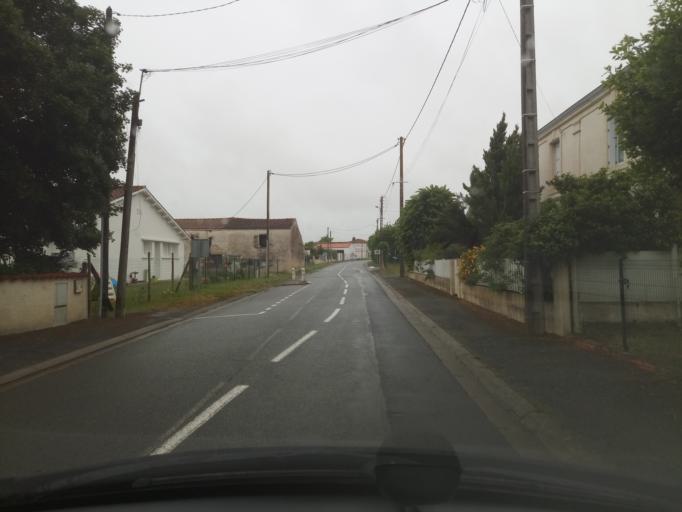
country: FR
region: Poitou-Charentes
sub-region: Departement de la Charente-Maritime
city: Andilly
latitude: 46.2326
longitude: -0.9991
